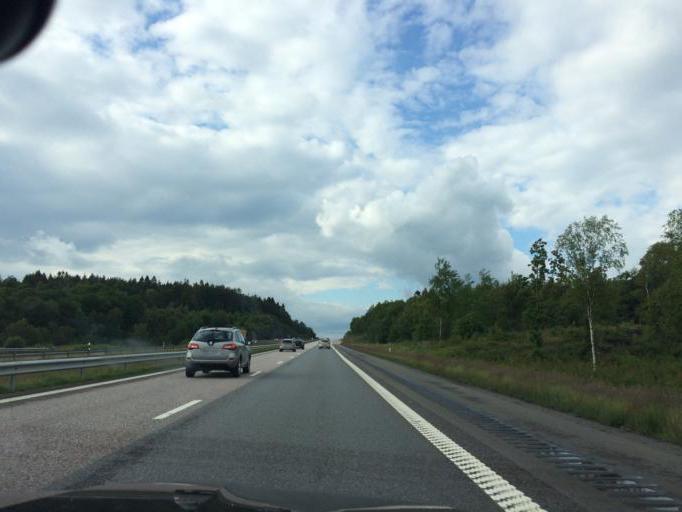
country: SE
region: Halland
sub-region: Kungsbacka Kommun
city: Frillesas
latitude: 57.3282
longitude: 12.2068
